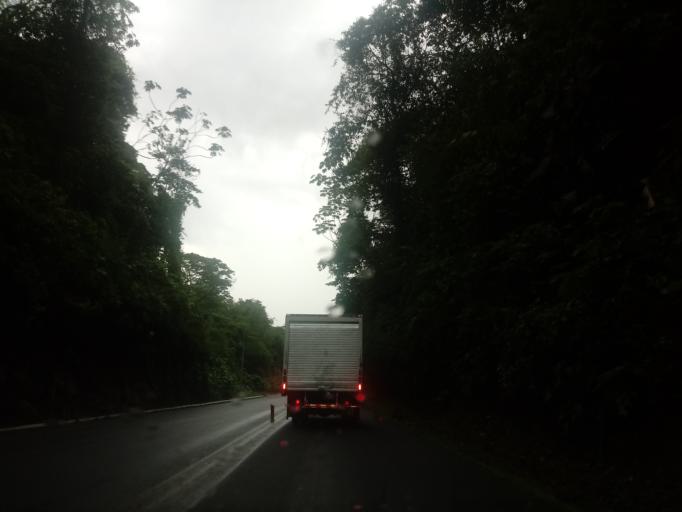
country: CR
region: San Jose
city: Dulce Nombre de Jesus
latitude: 10.1978
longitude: -83.9019
